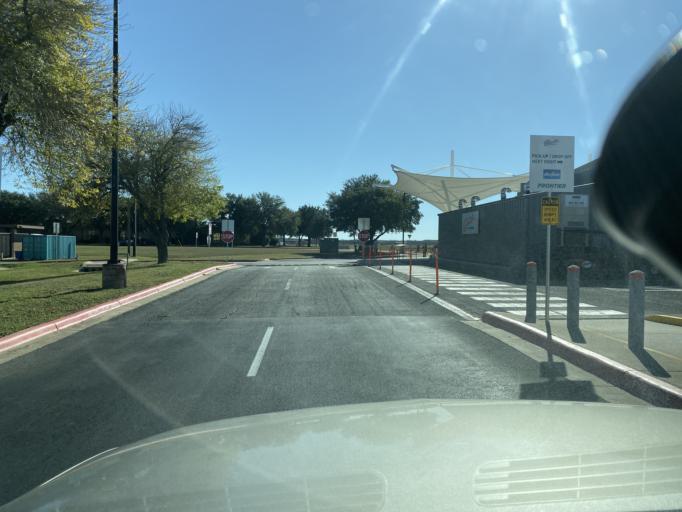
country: US
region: Texas
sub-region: Travis County
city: Hornsby Bend
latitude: 30.1936
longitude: -97.6703
